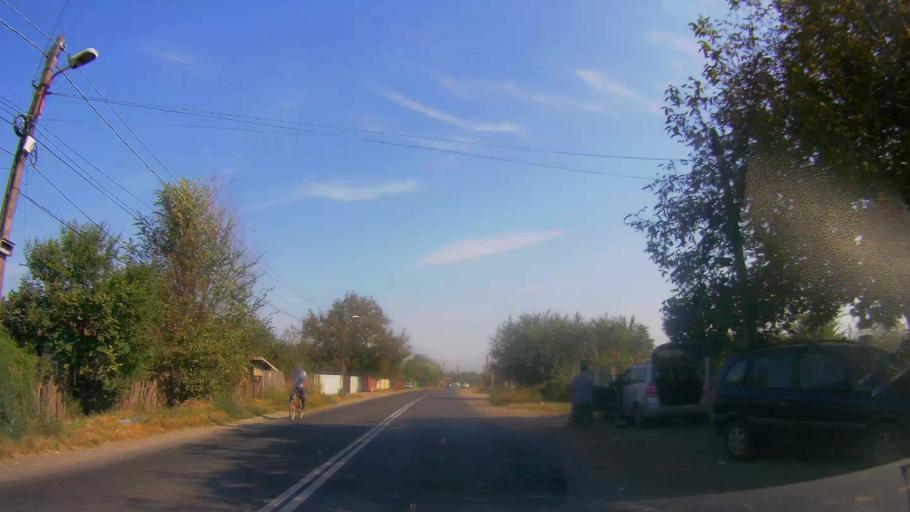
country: RO
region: Giurgiu
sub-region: Comuna Fratesti
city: Remus
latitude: 43.9112
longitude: 25.9834
